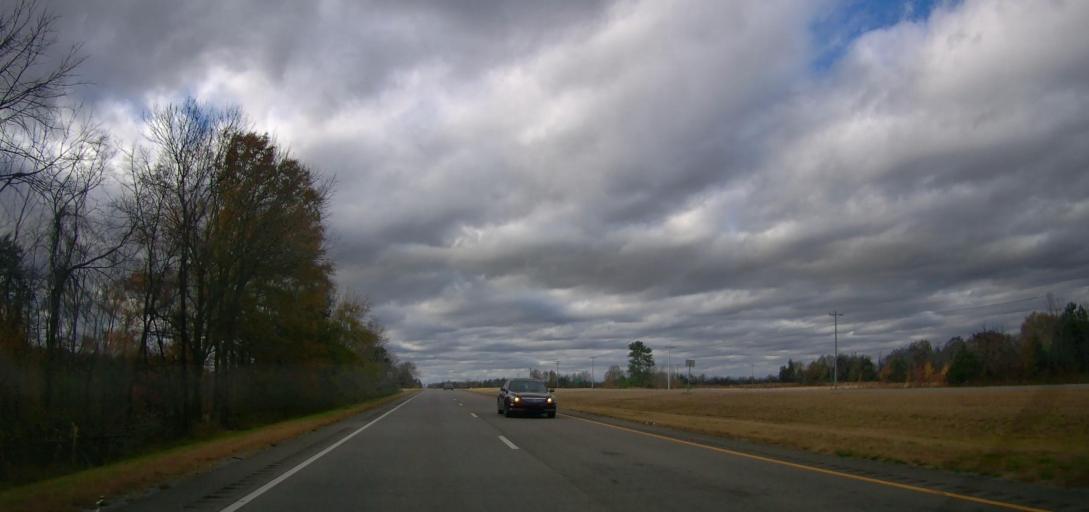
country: US
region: Alabama
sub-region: Morgan County
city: Danville
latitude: 34.3777
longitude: -87.0904
